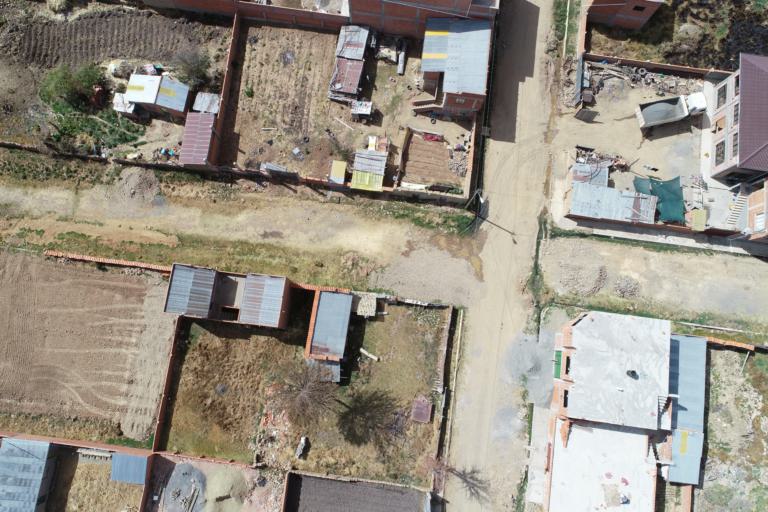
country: BO
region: La Paz
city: Huatajata
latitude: -16.1914
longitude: -68.7458
